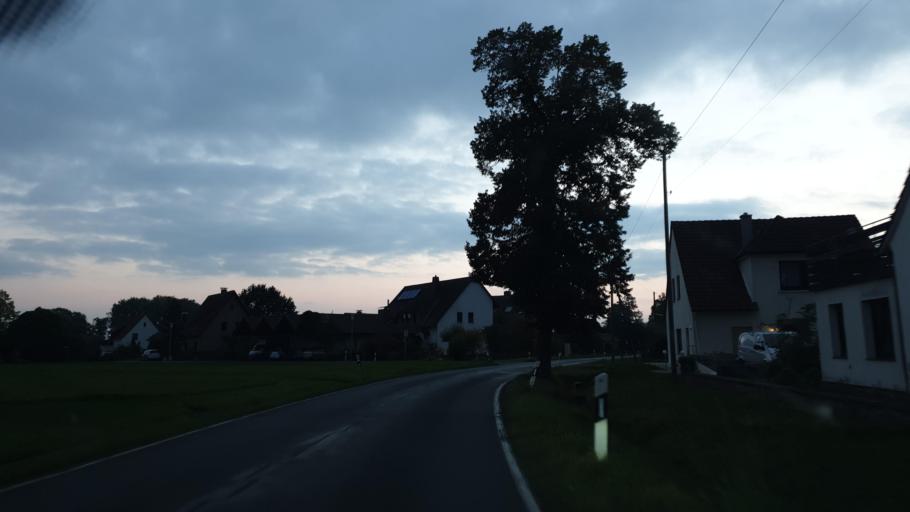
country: DE
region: North Rhine-Westphalia
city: Loehne
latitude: 52.2369
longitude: 8.7012
